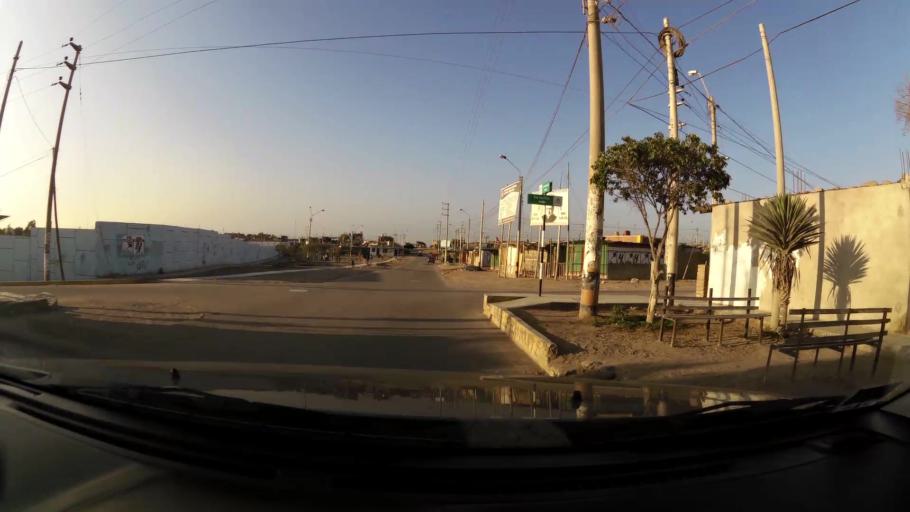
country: PE
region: Ica
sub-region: Provincia de Pisco
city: Villa Tupac Amaru
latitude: -13.7115
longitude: -76.1466
